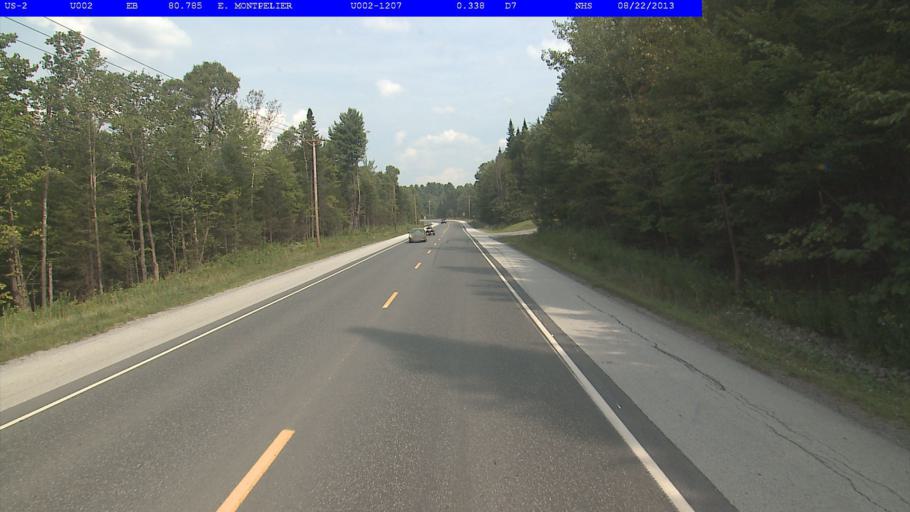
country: US
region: Vermont
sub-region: Washington County
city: Barre
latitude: 44.2424
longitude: -72.5113
